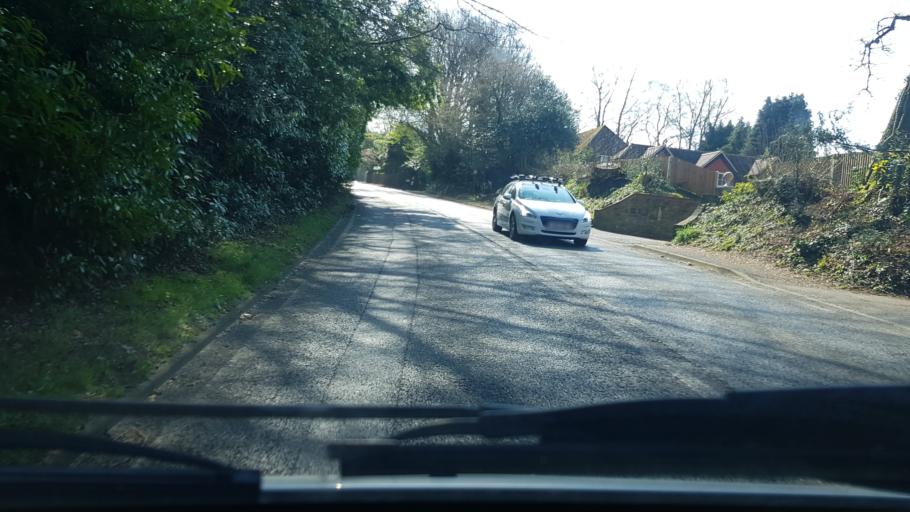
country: GB
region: England
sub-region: West Sussex
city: Fernhurst
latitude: 51.0666
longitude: -0.7232
